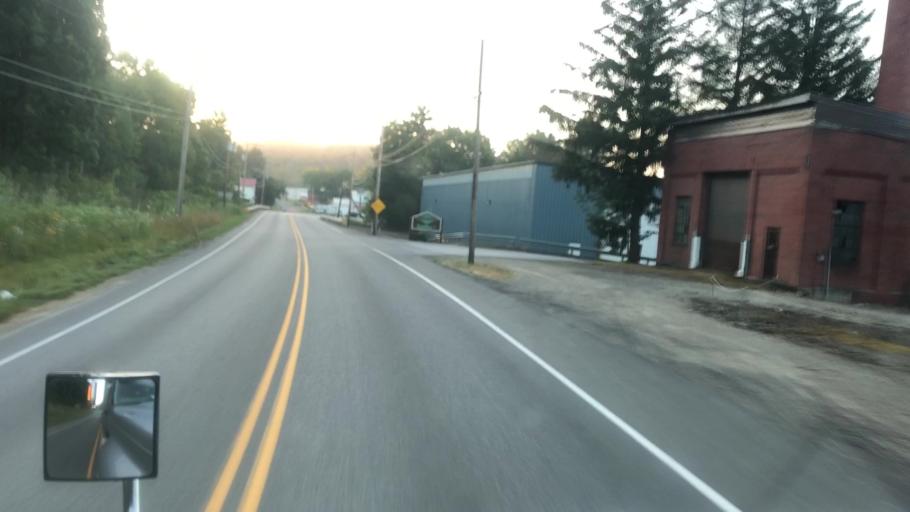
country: US
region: Pennsylvania
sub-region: Crawford County
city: Titusville
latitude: 41.6223
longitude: -79.6449
